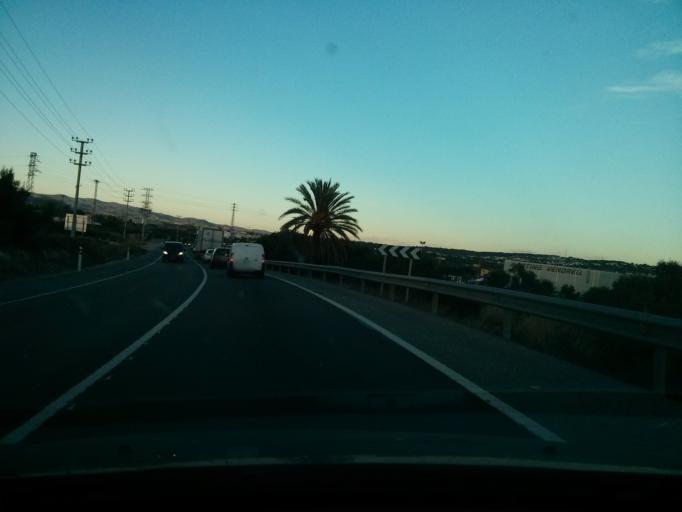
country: ES
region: Catalonia
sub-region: Provincia de Tarragona
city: El Vendrell
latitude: 41.1974
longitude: 1.5275
